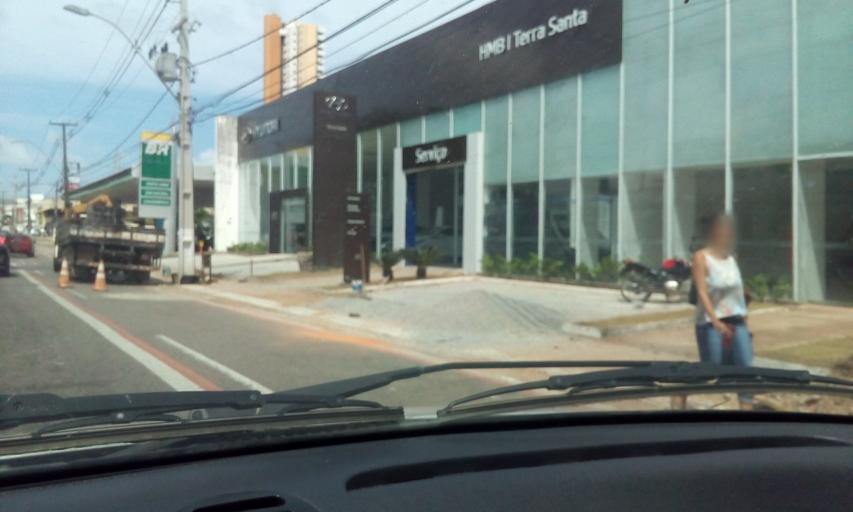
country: BR
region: Rio Grande do Norte
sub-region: Natal
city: Natal
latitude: -5.8175
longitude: -35.2120
